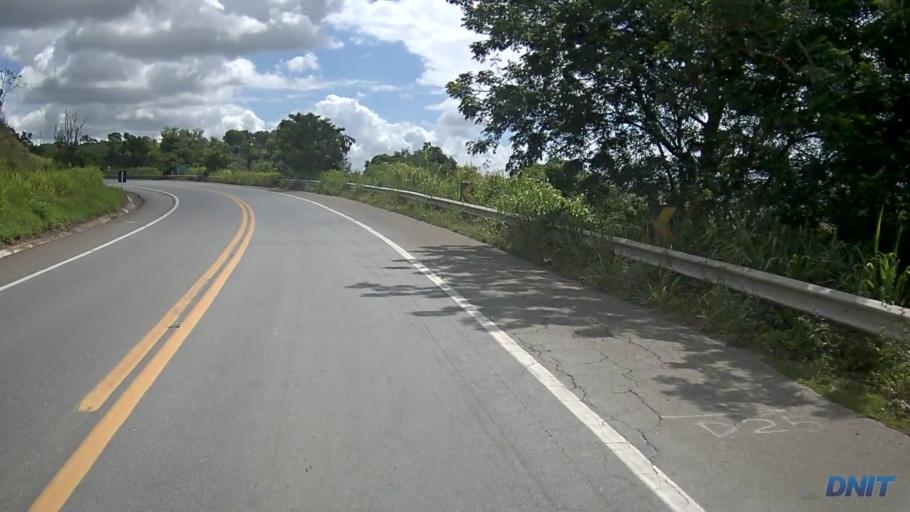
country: BR
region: Minas Gerais
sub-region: Governador Valadares
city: Governador Valadares
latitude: -18.9622
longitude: -42.0767
